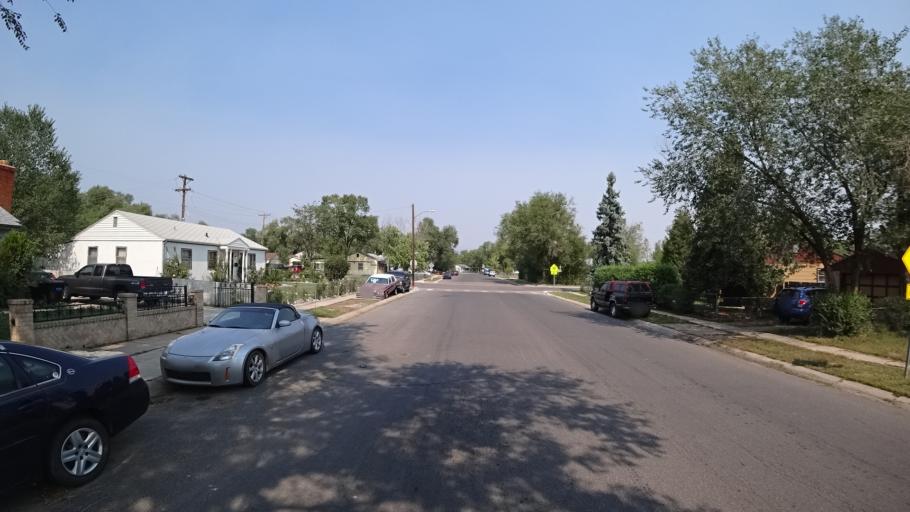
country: US
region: Colorado
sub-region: El Paso County
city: Colorado Springs
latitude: 38.8051
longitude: -104.8168
